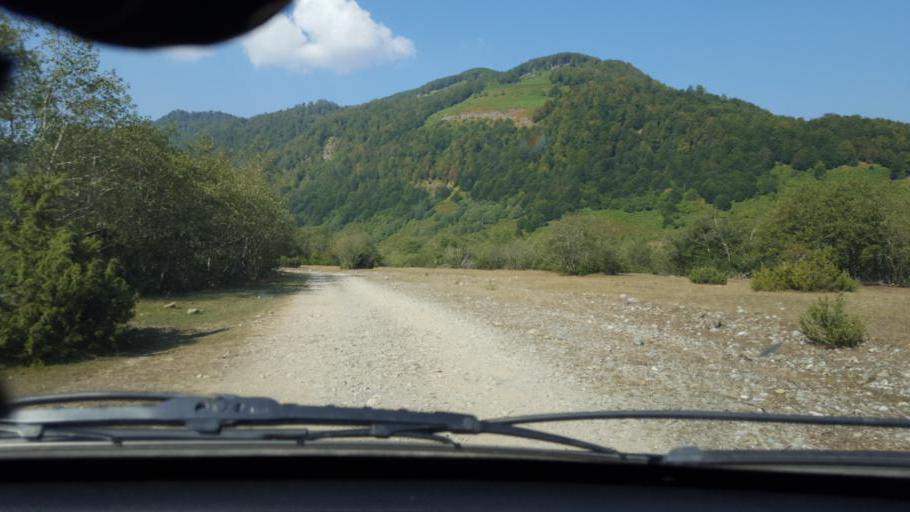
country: ME
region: Andrijevica
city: Andrijevica
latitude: 42.5976
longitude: 19.6584
